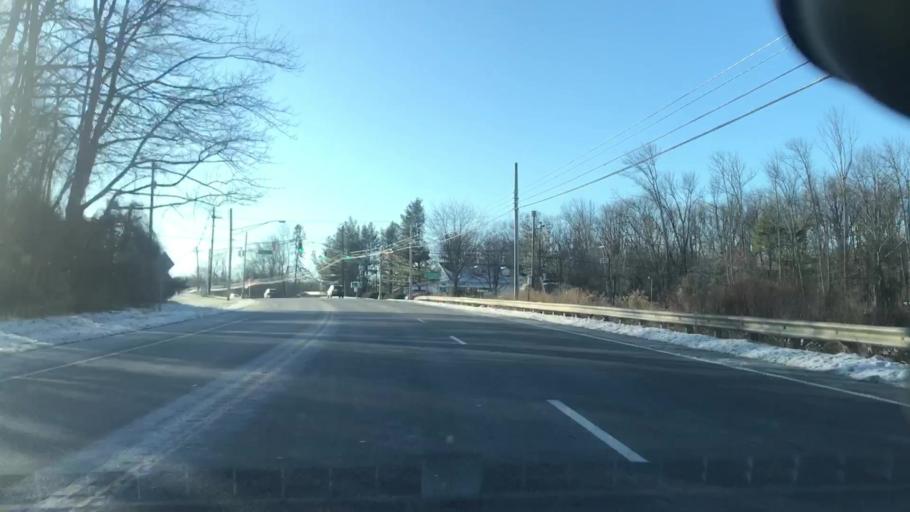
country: US
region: New Jersey
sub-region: Morris County
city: Chester
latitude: 40.8043
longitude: -74.7147
